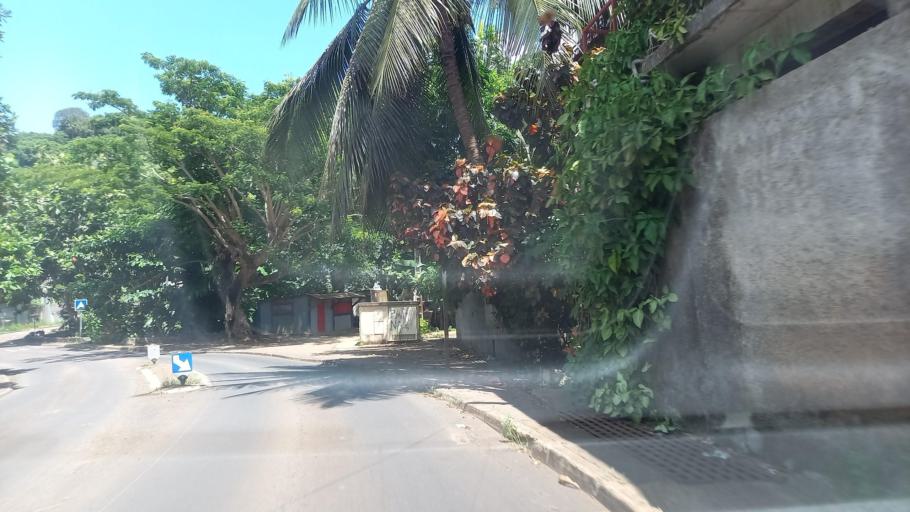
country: YT
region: Chirongui
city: Chirongui
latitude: -12.8907
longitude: 45.1392
